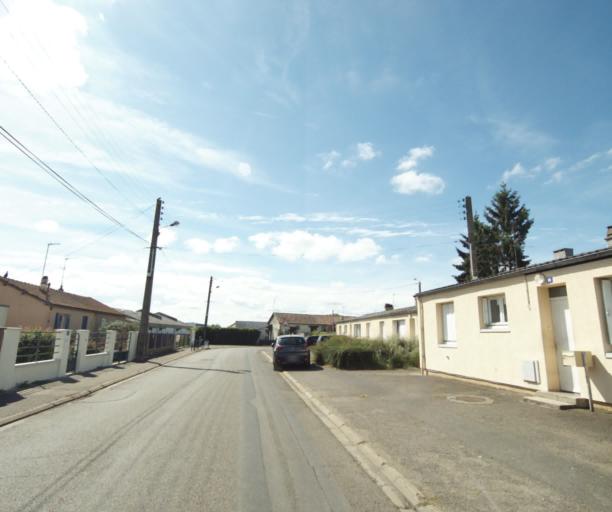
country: FR
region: Centre
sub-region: Departement d'Eure-et-Loir
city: Luce
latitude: 48.4308
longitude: 1.4532
